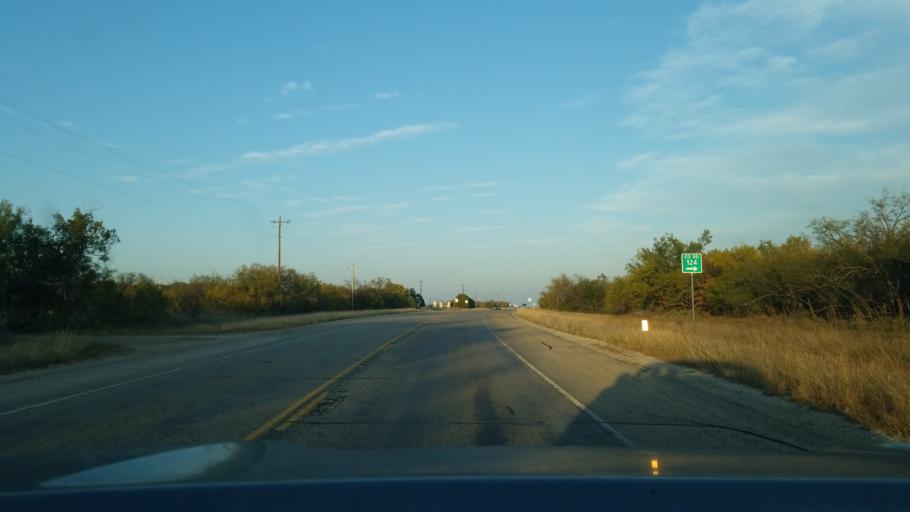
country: US
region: Texas
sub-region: Eastland County
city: Cisco
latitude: 32.3962
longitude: -98.9703
